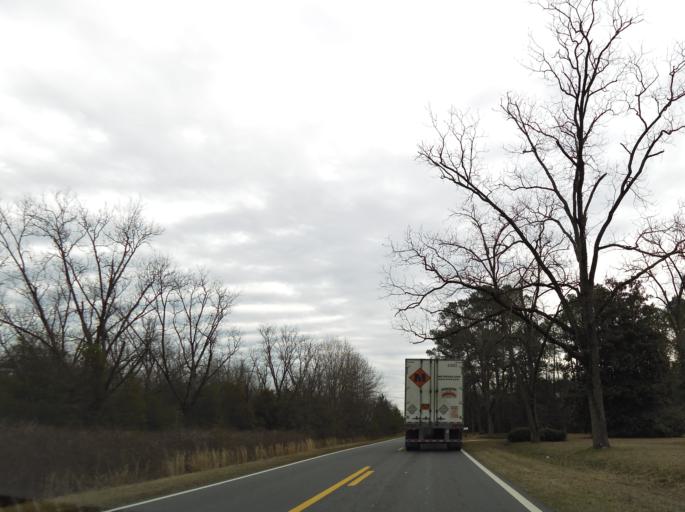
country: US
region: Georgia
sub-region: Houston County
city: Centerville
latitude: 32.6917
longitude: -83.6700
